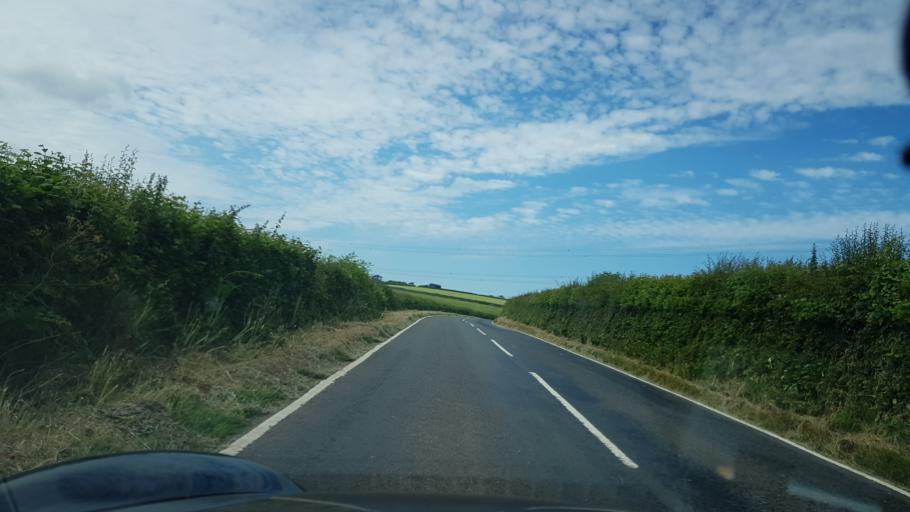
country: GB
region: Wales
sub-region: Carmarthenshire
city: Whitland
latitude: 51.7790
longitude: -4.6224
